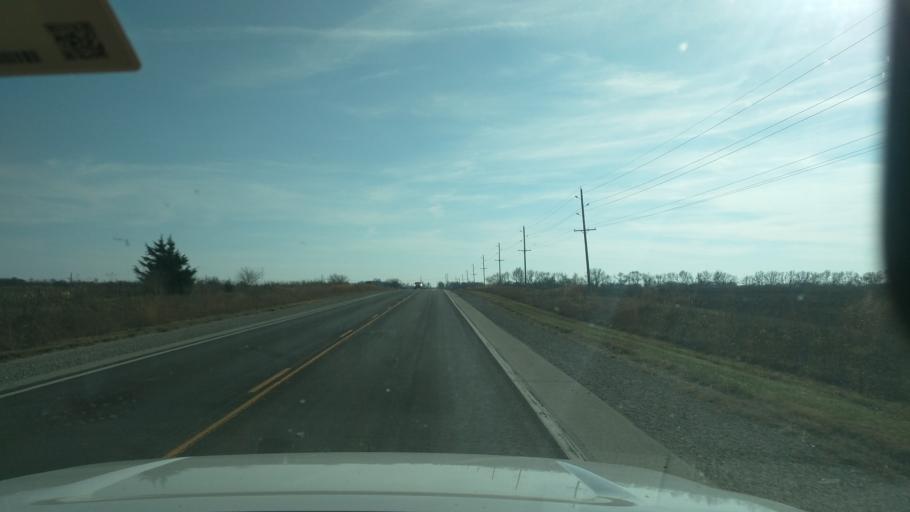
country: US
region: Kansas
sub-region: Lyon County
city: Emporia
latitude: 38.2999
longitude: -96.1804
